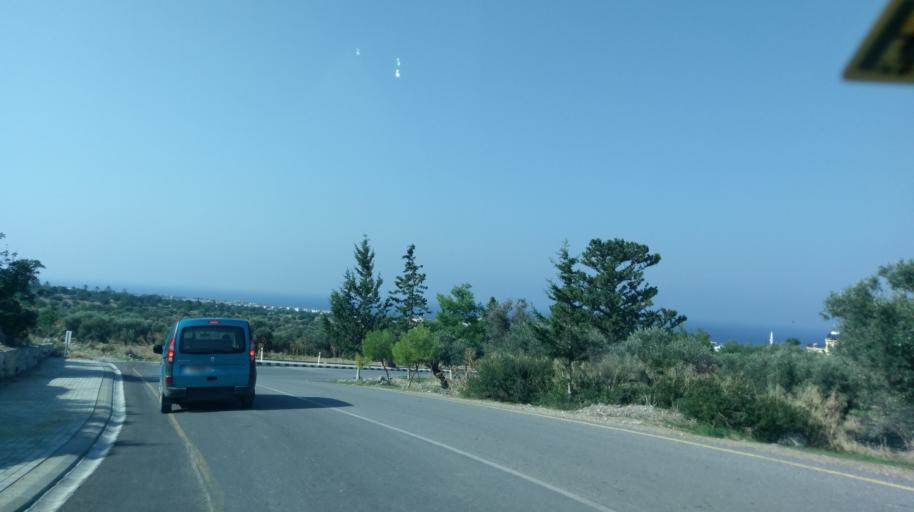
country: CY
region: Ammochostos
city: Lefkonoiko
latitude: 35.3894
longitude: 33.7505
